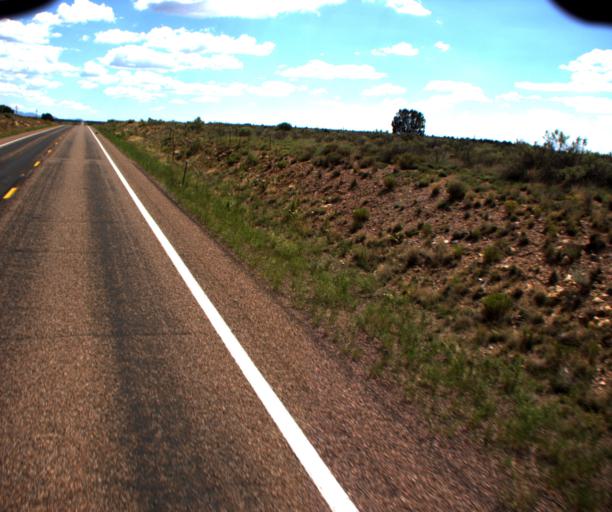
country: US
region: Arizona
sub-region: Coconino County
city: Williams
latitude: 35.5851
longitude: -112.1512
